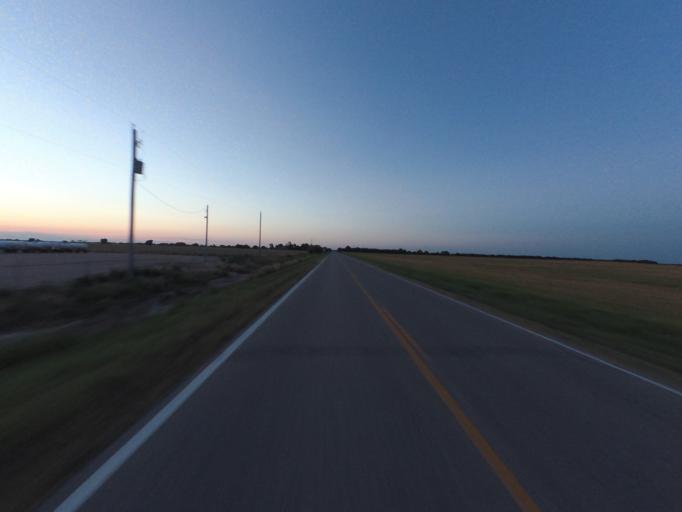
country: US
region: Kansas
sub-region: Reno County
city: Nickerson
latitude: 38.0592
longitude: -98.0875
